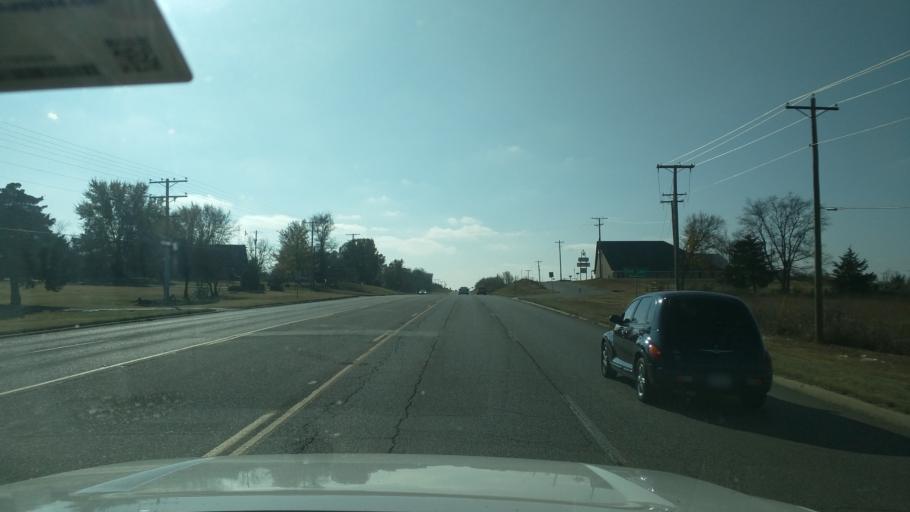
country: US
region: Oklahoma
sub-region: Washington County
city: Bartlesville
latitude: 36.6966
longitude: -95.9352
